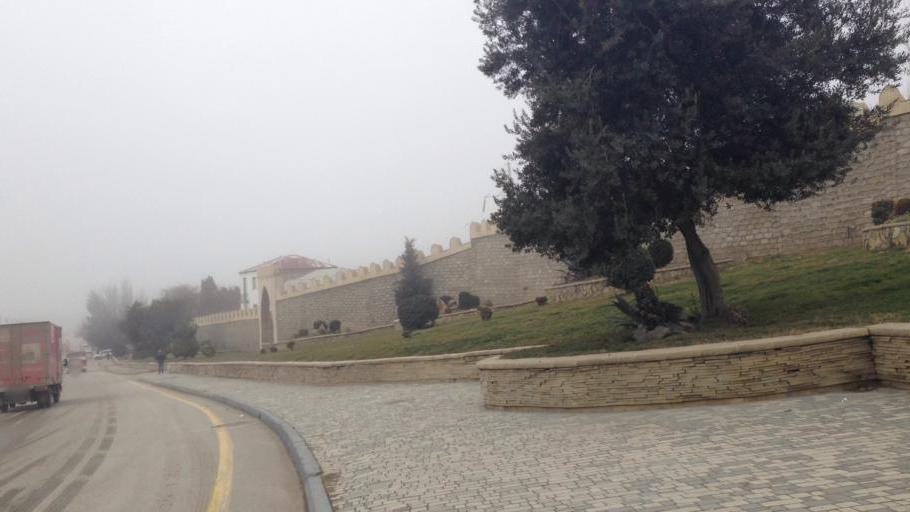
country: AZ
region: Baki
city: Qaracuxur
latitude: 40.3526
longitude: 49.9587
